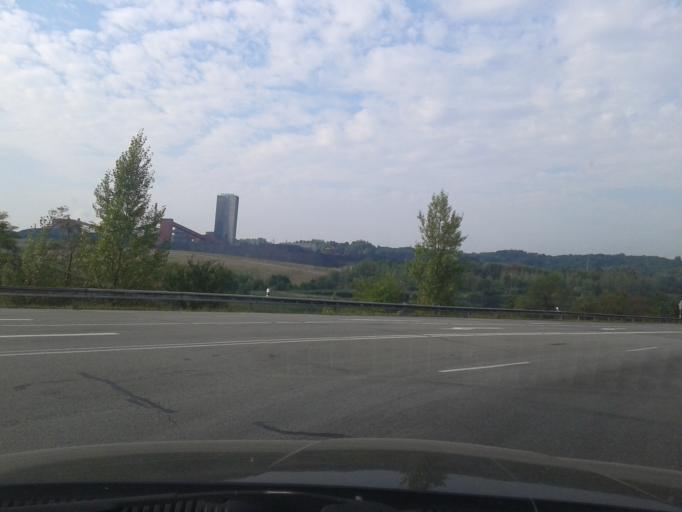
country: CZ
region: Moravskoslezsky
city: Orlova
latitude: 49.8387
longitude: 18.4459
